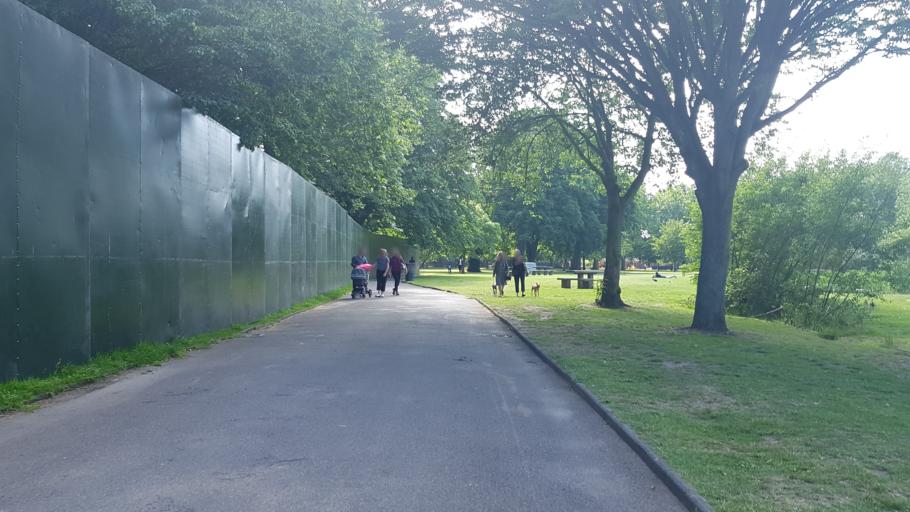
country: GB
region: England
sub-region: Greater London
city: Hackney
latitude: 51.5380
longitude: -0.0380
